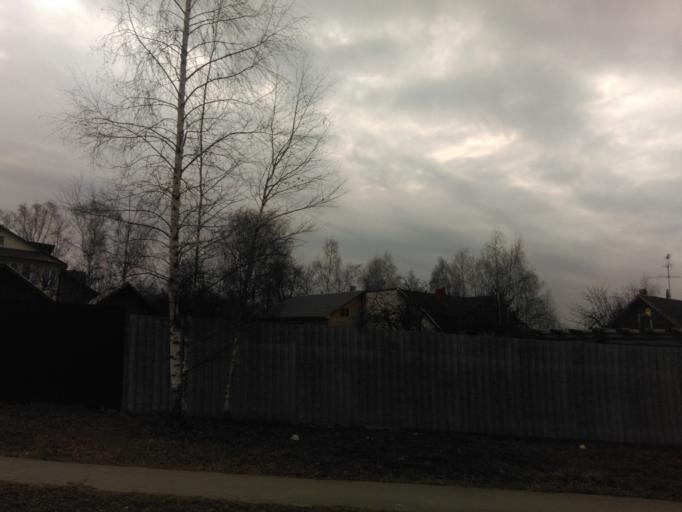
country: RU
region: Moskovskaya
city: Nikolina Gora
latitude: 55.7186
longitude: 37.0741
